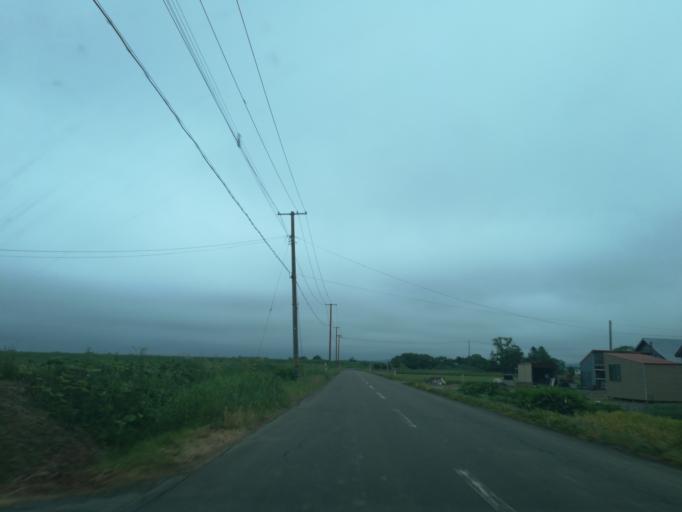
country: JP
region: Hokkaido
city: Iwamizawa
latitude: 43.1273
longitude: 141.6935
